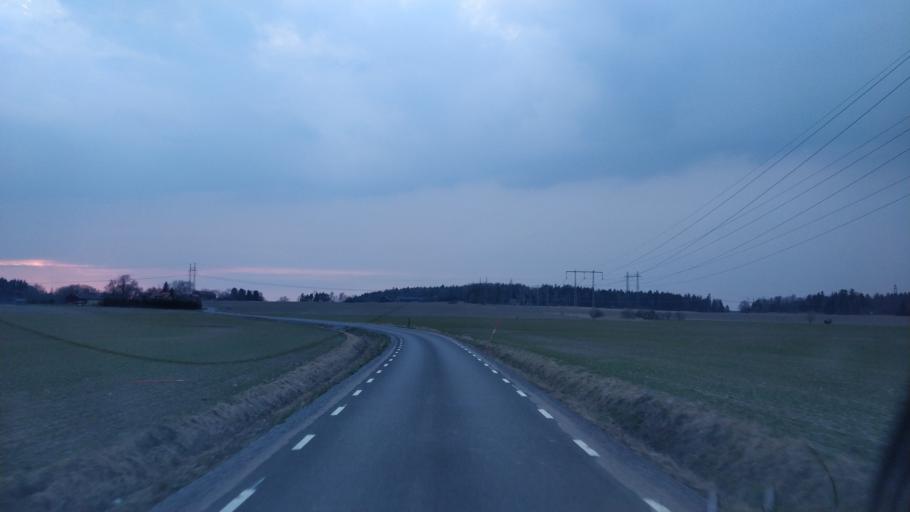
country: SE
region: Uppsala
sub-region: Enkopings Kommun
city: Orsundsbro
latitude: 59.7196
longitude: 17.2394
